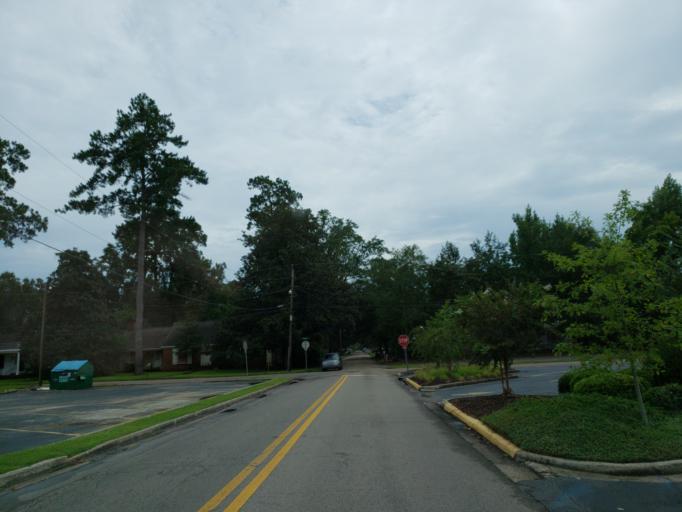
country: US
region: Mississippi
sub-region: Forrest County
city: Hattiesburg
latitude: 31.3233
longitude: -89.3131
